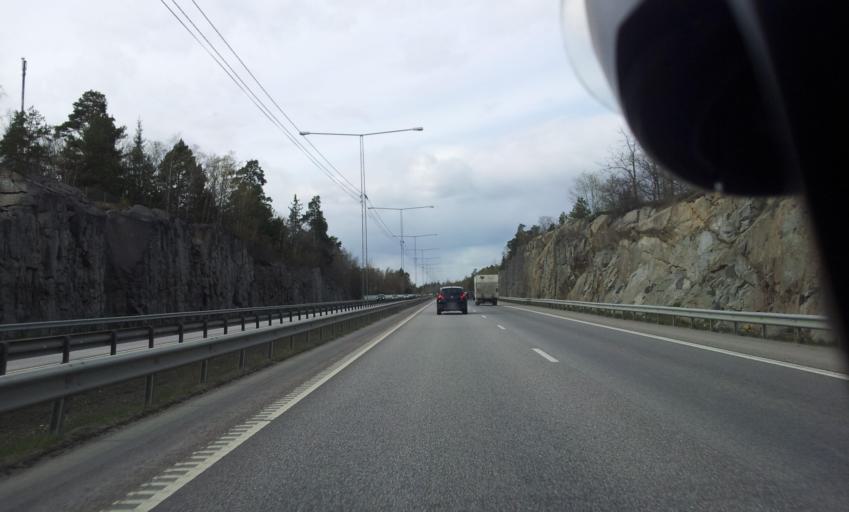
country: SE
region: Stockholm
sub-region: Jarfalla Kommun
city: Jakobsberg
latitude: 59.4585
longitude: 17.8274
